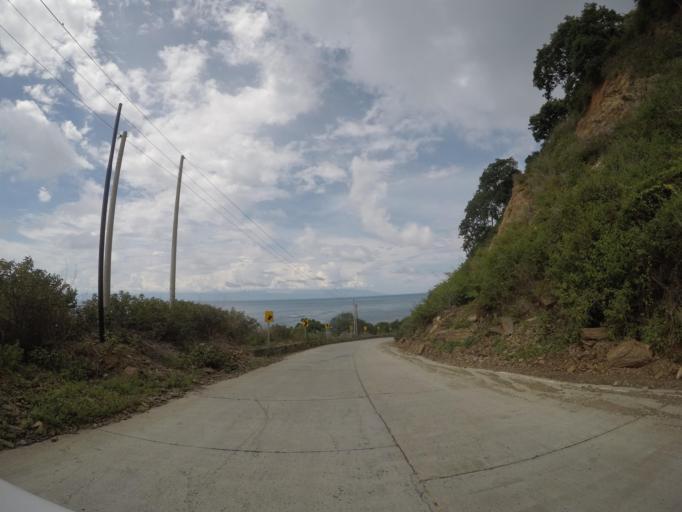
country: TL
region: Liquica
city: Maubara
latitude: -8.6709
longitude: 125.1086
